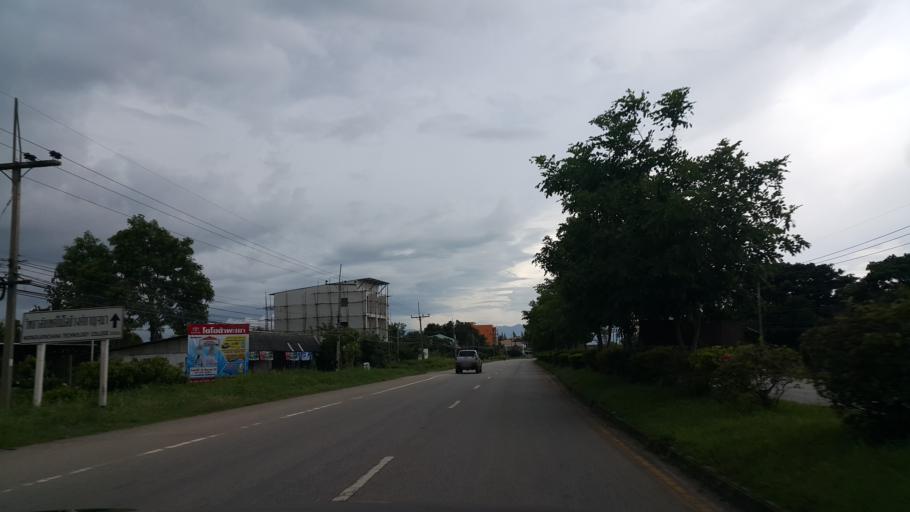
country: TH
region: Phayao
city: Dok Kham Tai
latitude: 19.1609
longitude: 99.9715
